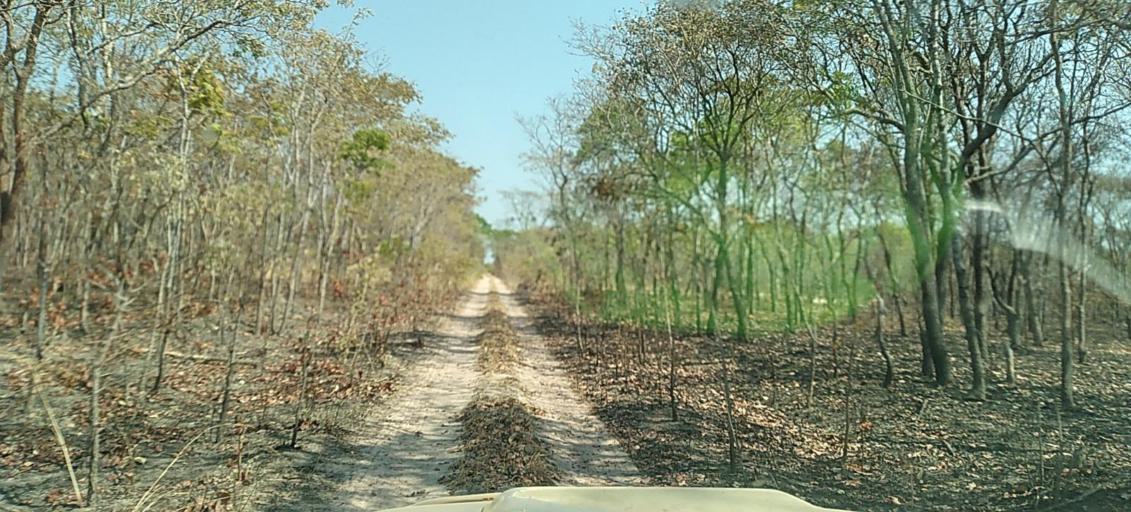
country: ZM
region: North-Western
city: Kalengwa
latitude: -13.3226
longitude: 24.8241
